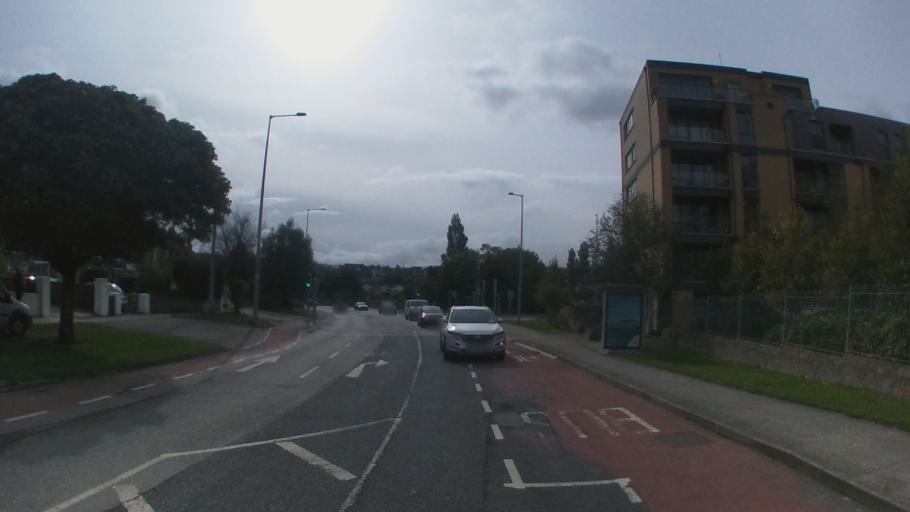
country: IE
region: Leinster
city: Cabinteely
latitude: 53.2673
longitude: -6.1483
